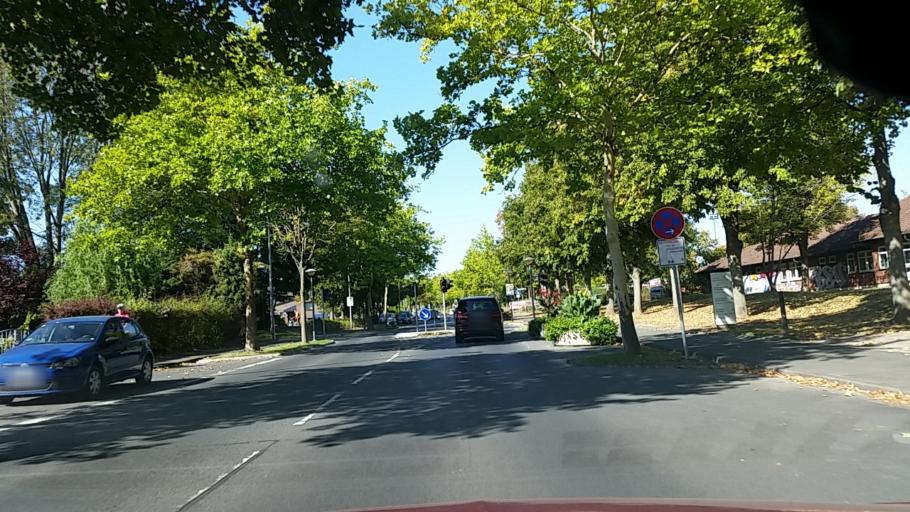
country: DE
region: Hesse
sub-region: Regierungsbezirk Kassel
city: Baunatal
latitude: 51.2556
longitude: 9.4042
